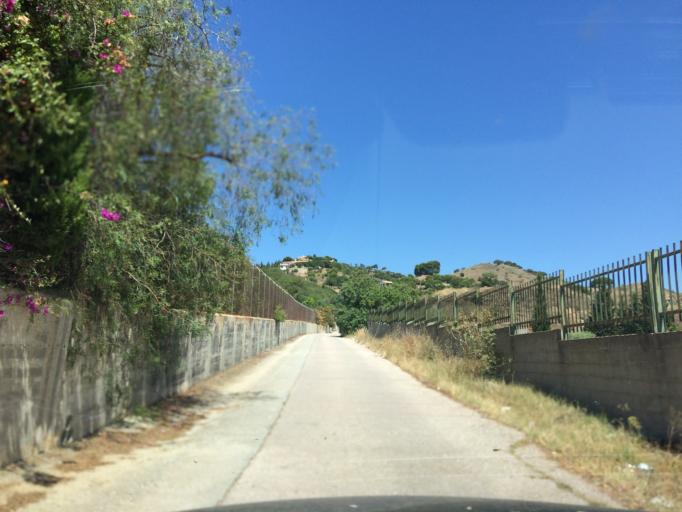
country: ES
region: Andalusia
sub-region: Provincia de Malaga
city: Malaga
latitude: 36.7363
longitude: -4.4658
